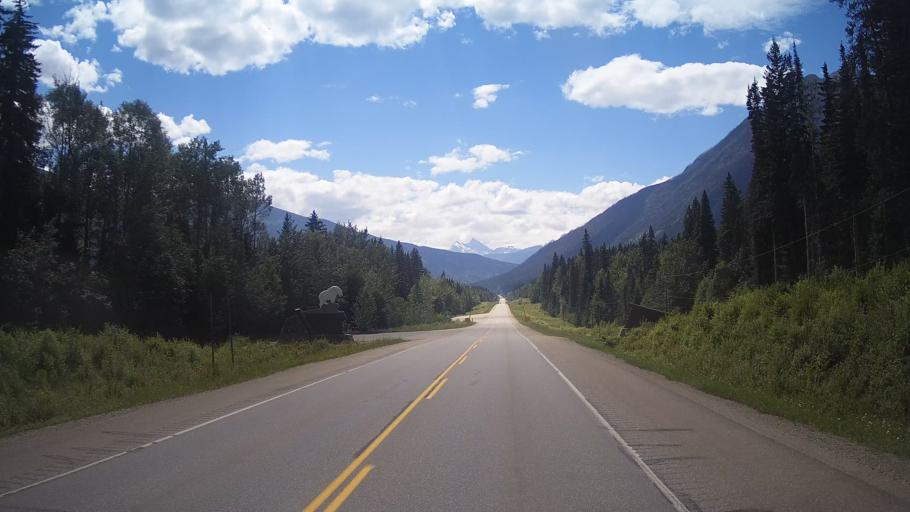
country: CA
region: Alberta
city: Grande Cache
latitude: 53.0280
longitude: -119.2607
